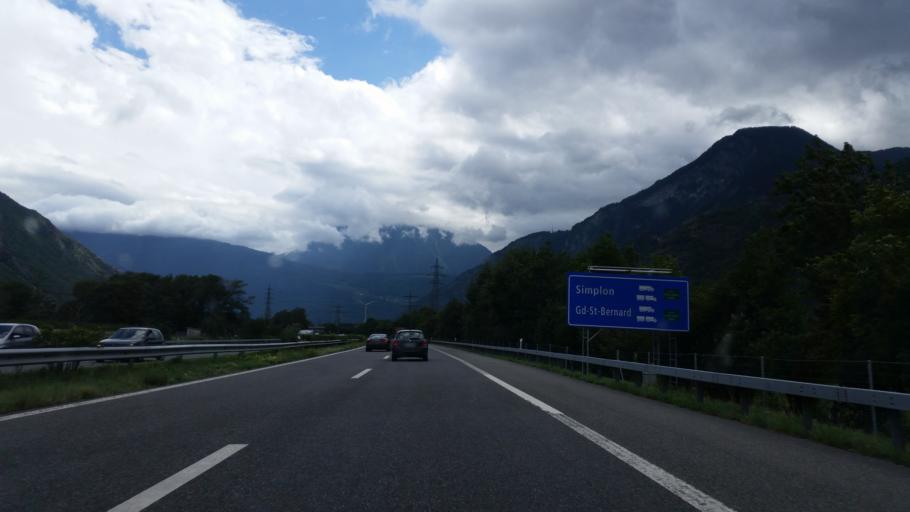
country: CH
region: Valais
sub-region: Saint-Maurice District
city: Vernayaz
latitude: 46.1457
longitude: 7.0347
